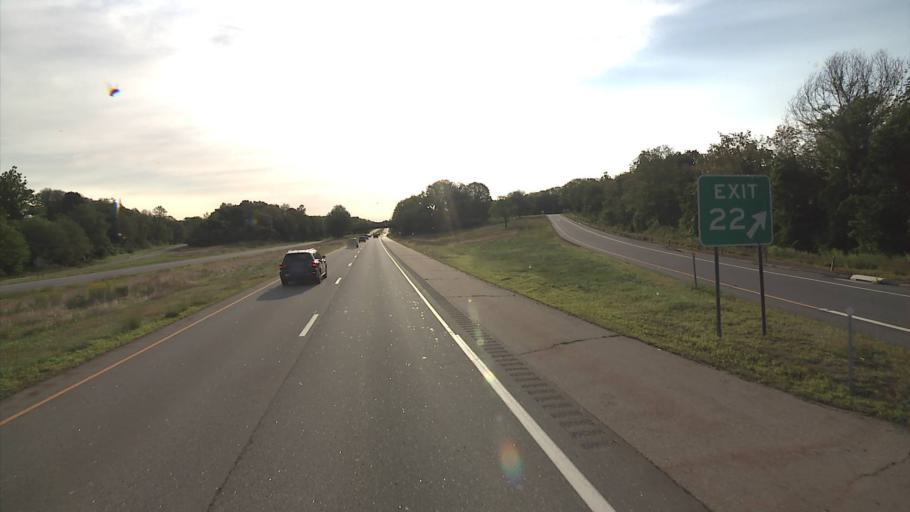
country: US
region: Connecticut
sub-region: New London County
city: Montville Center
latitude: 41.5695
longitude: -72.2121
